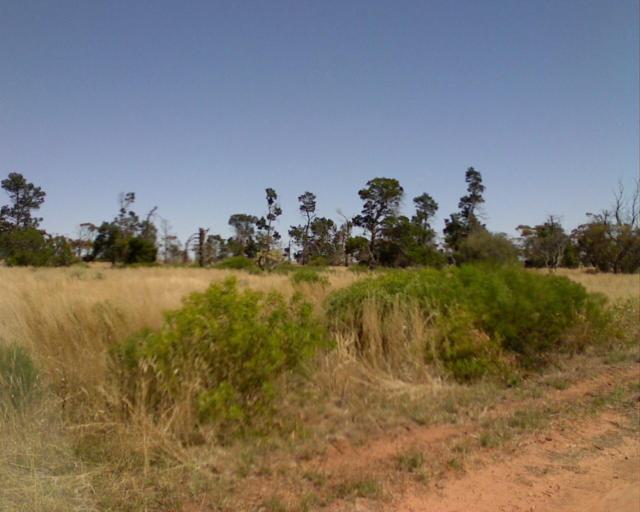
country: AU
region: South Australia
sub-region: Kimba
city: Caralue
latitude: -33.1588
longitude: 135.8749
